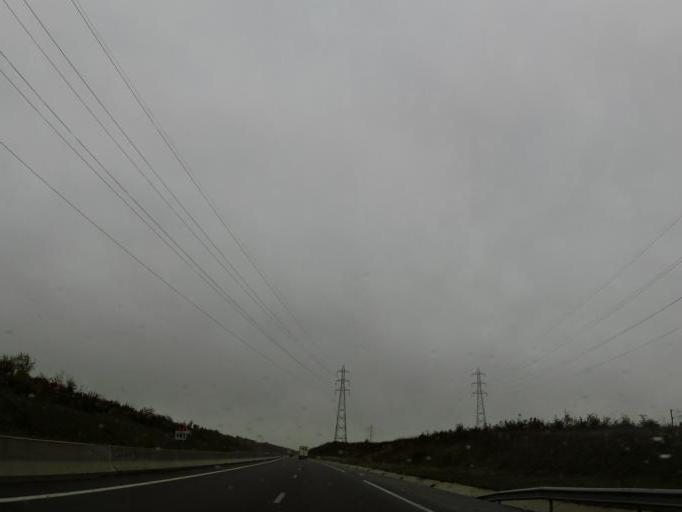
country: FR
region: Champagne-Ardenne
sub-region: Departement de la Marne
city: Cormontreuil
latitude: 49.2087
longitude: 4.0382
